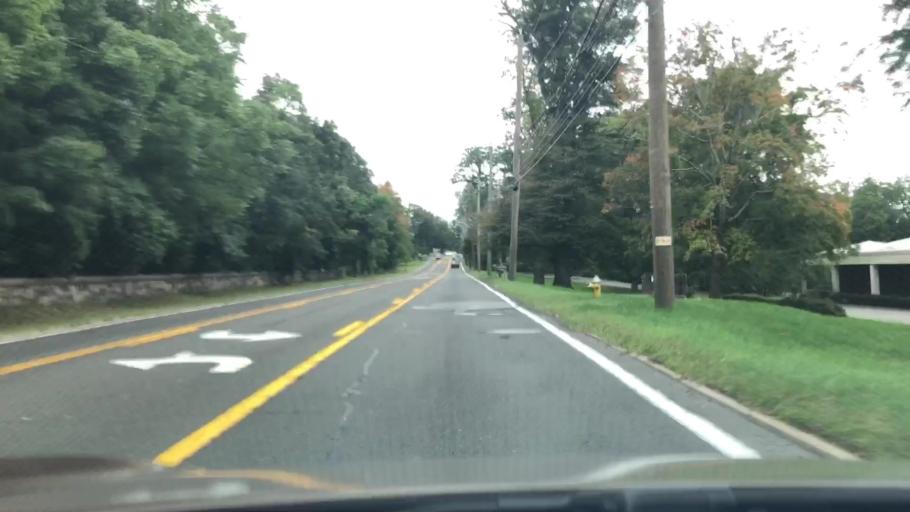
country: US
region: New York
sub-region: Westchester County
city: Ossining
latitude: 41.1274
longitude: -73.8617
